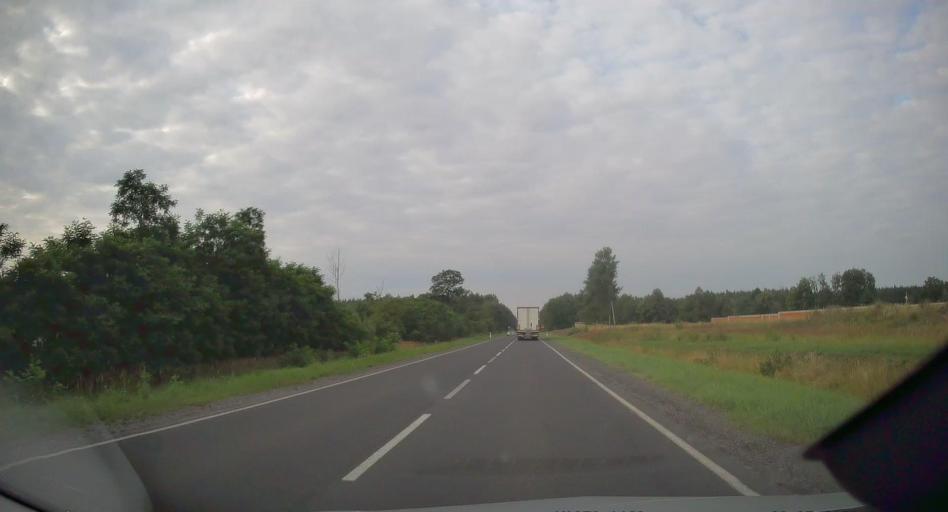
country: PL
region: Lodz Voivodeship
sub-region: Powiat radomszczanski
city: Plawno
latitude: 50.9930
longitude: 19.4151
